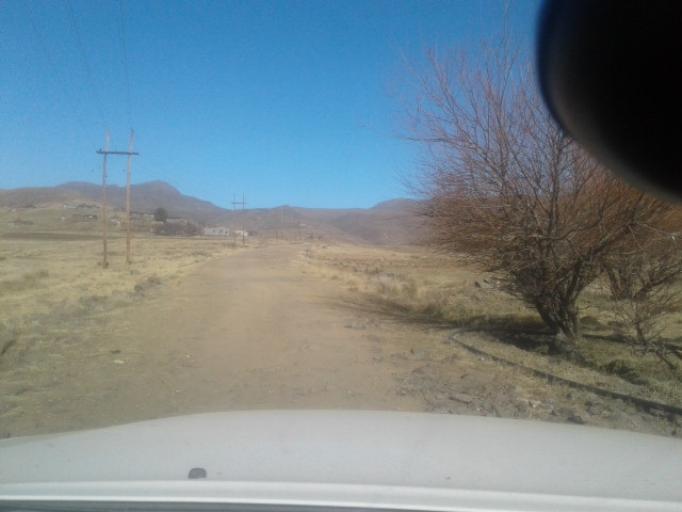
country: LS
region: Maseru
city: Nako
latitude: -29.3783
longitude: 28.0163
